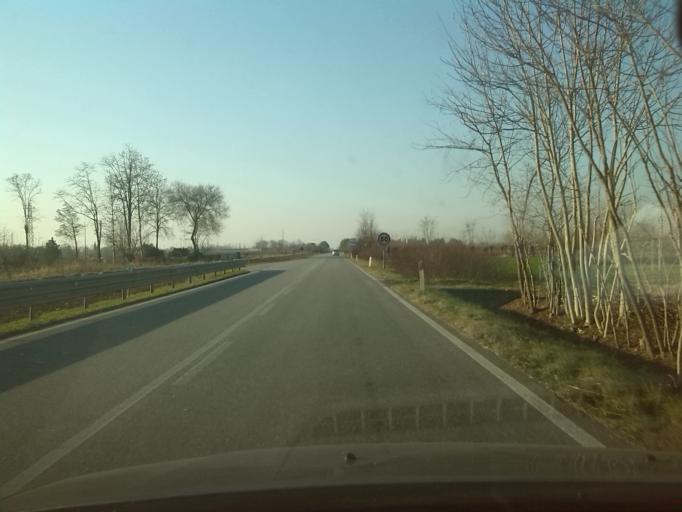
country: IT
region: Friuli Venezia Giulia
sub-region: Provincia di Udine
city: Castions di Strada
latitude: 45.9173
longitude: 13.2001
